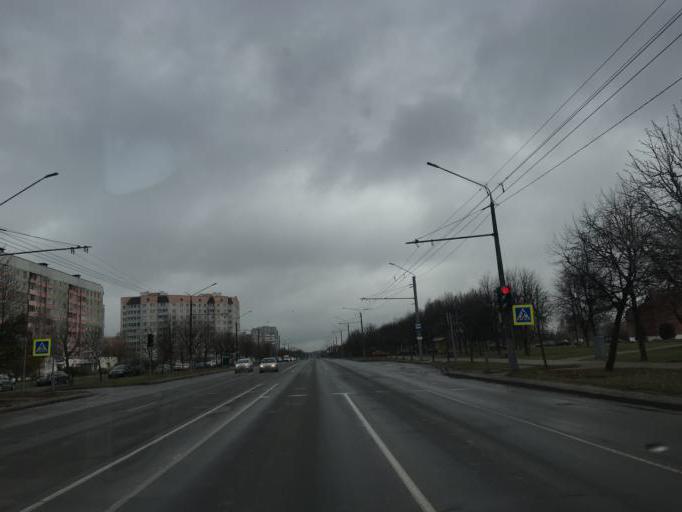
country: BY
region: Mogilev
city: Mahilyow
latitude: 53.8691
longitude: 30.3261
